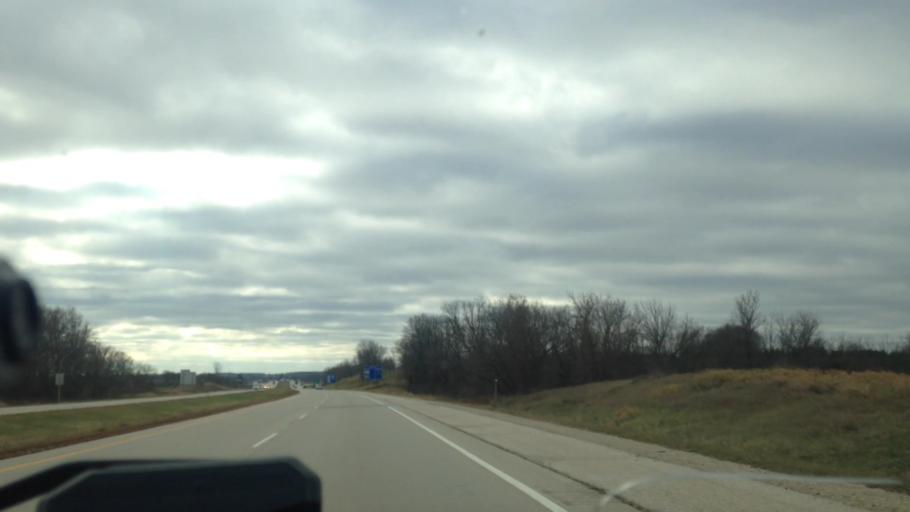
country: US
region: Wisconsin
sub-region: Washington County
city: Jackson
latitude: 43.3366
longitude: -88.1902
